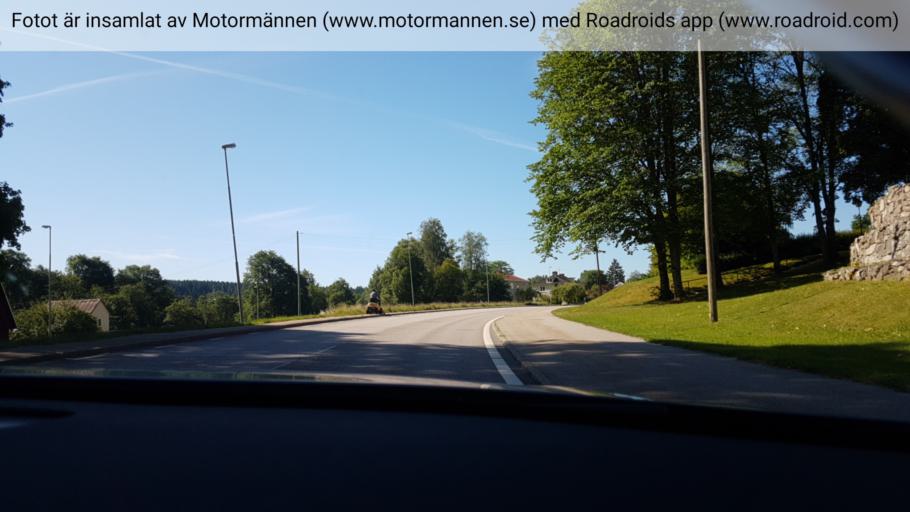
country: SE
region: Vaestra Goetaland
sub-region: Ulricehamns Kommun
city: Ulricehamn
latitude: 57.9272
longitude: 13.4936
